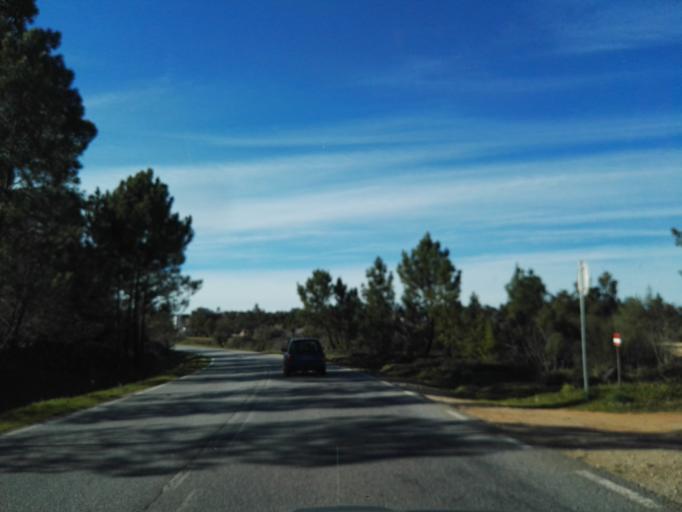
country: PT
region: Santarem
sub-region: Abrantes
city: Alferrarede
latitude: 39.4746
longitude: -8.0726
